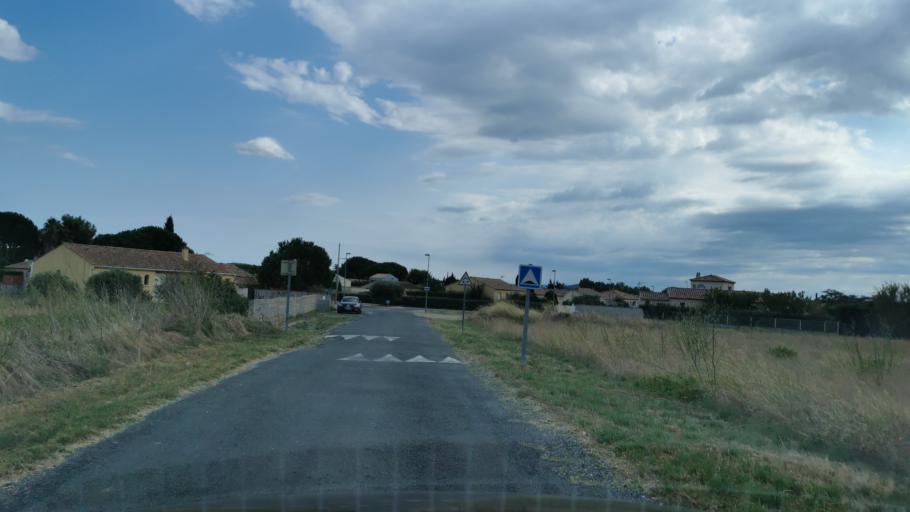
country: FR
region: Languedoc-Roussillon
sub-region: Departement de l'Aude
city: Saint-Marcel-sur-Aude
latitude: 43.2522
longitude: 2.9201
